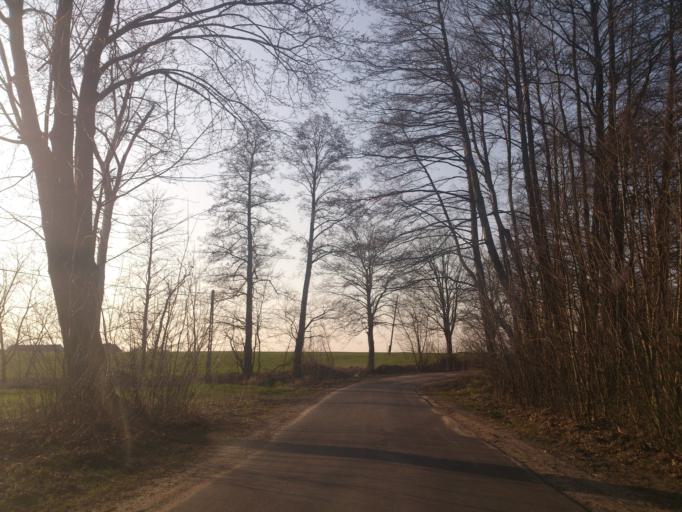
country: PL
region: Kujawsko-Pomorskie
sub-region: Powiat golubsko-dobrzynski
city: Radomin
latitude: 53.1160
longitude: 19.1373
